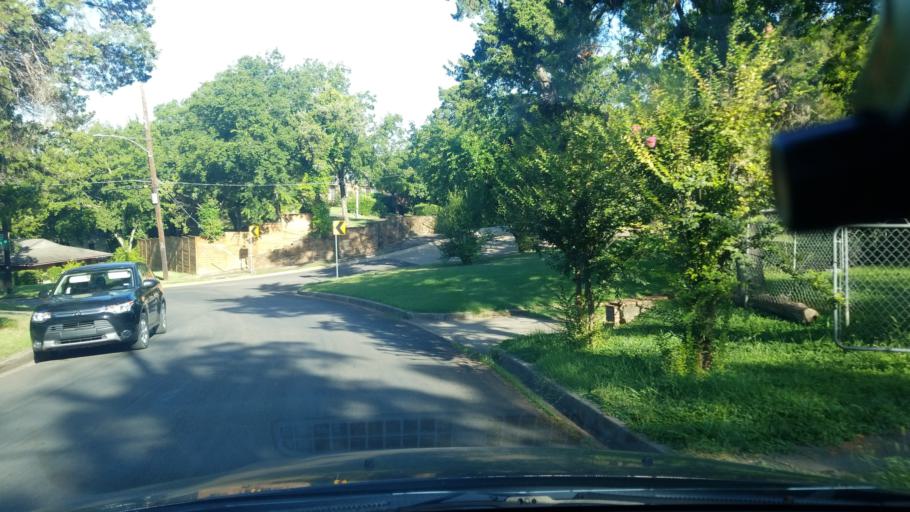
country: US
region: Texas
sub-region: Dallas County
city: Dallas
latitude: 32.7314
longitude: -96.8196
